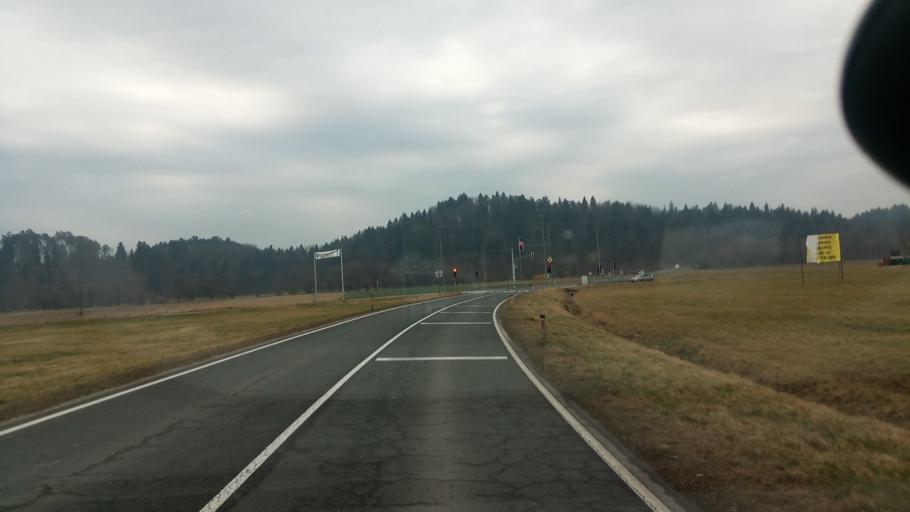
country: SI
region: Domzale
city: Vir
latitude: 46.1479
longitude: 14.6175
